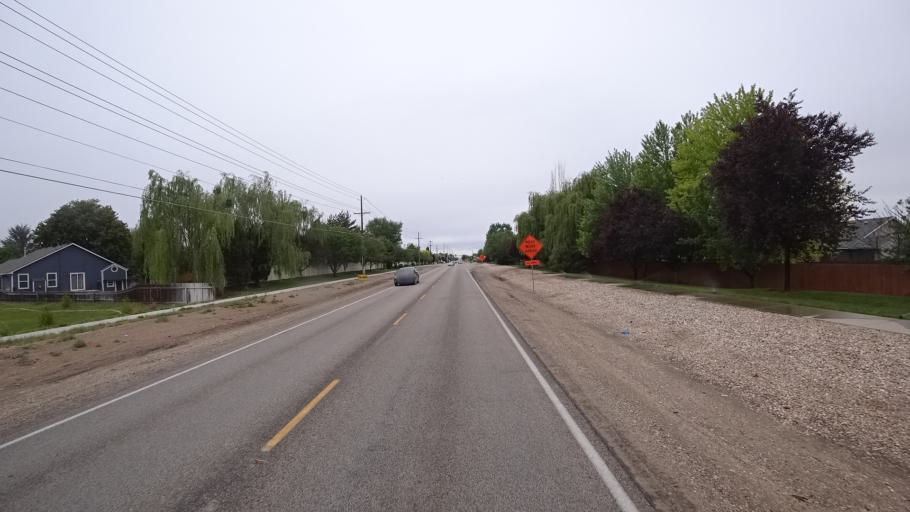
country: US
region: Idaho
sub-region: Ada County
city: Meridian
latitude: 43.6340
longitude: -116.4300
